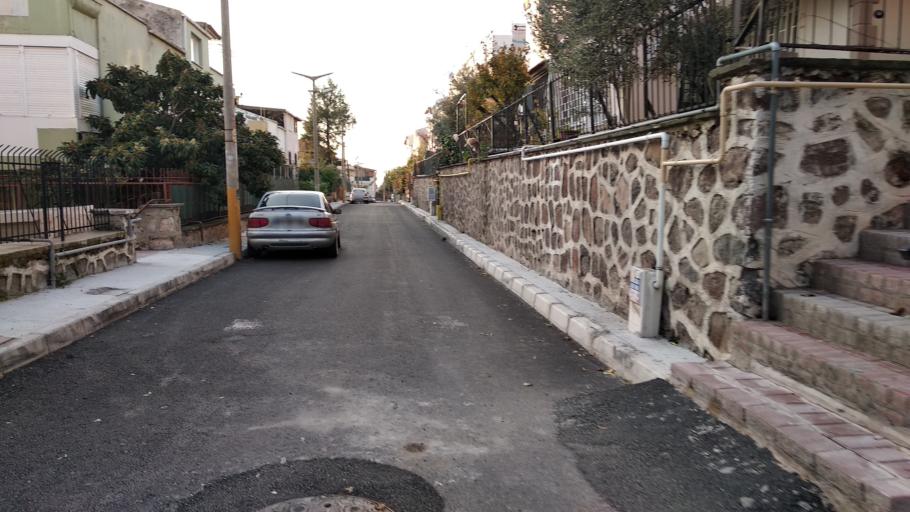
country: TR
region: Izmir
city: Karsiyaka
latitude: 38.4971
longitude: 27.0833
